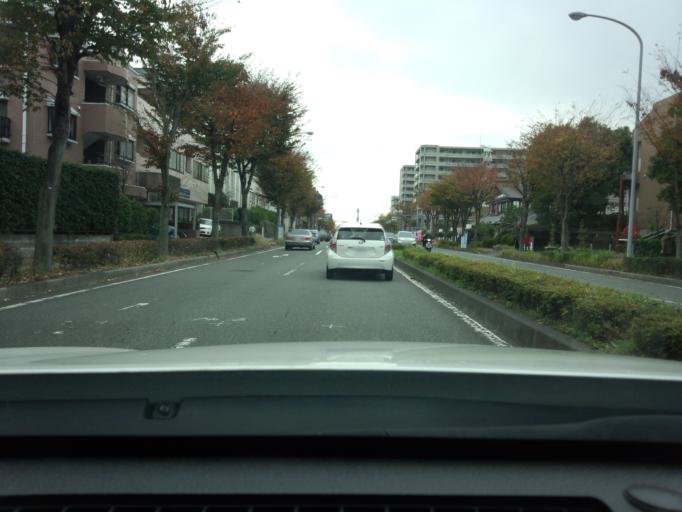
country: JP
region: Tokyo
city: Chofugaoka
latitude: 35.5580
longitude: 139.5784
